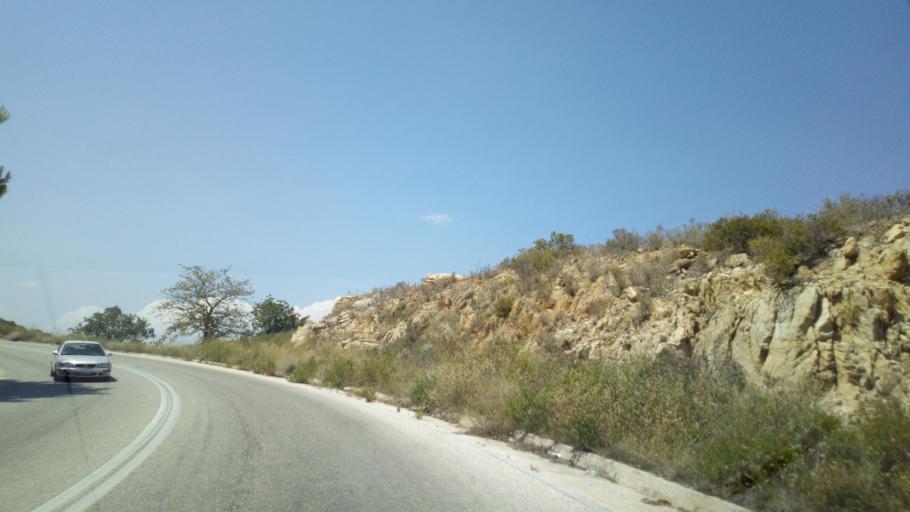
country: GR
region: Central Macedonia
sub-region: Nomos Chalkidikis
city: Sarti
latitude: 40.1561
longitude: 23.9106
